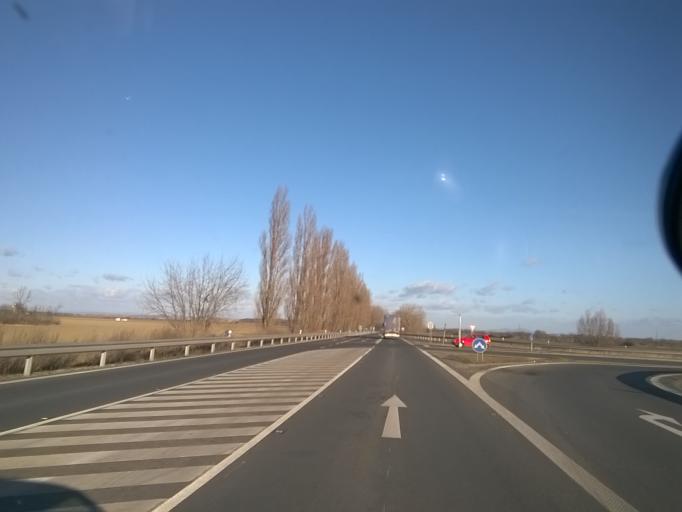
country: SK
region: Trnavsky
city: Sladkovicovo
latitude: 48.2130
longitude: 17.6464
